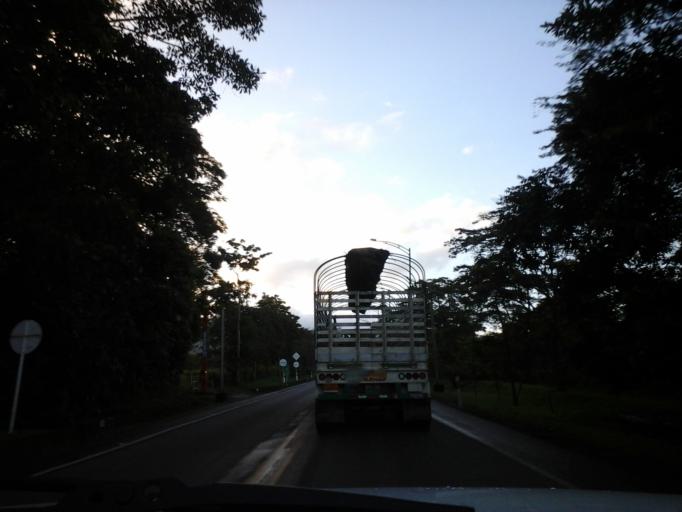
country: CO
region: Meta
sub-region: Villavicencio
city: Villavicencio
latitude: 4.1322
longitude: -73.6548
